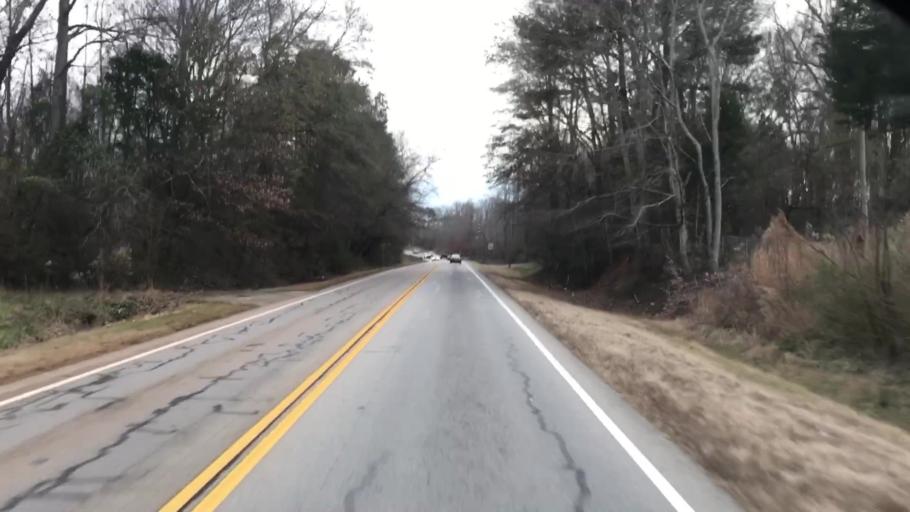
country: US
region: Georgia
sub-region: Jackson County
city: Hoschton
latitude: 34.0534
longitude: -83.7795
